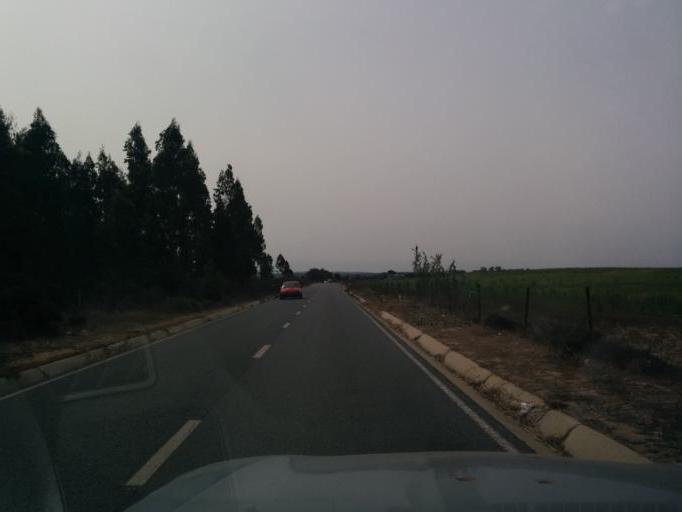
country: PT
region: Beja
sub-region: Odemira
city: Sao Teotonio
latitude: 37.5996
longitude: -8.7440
